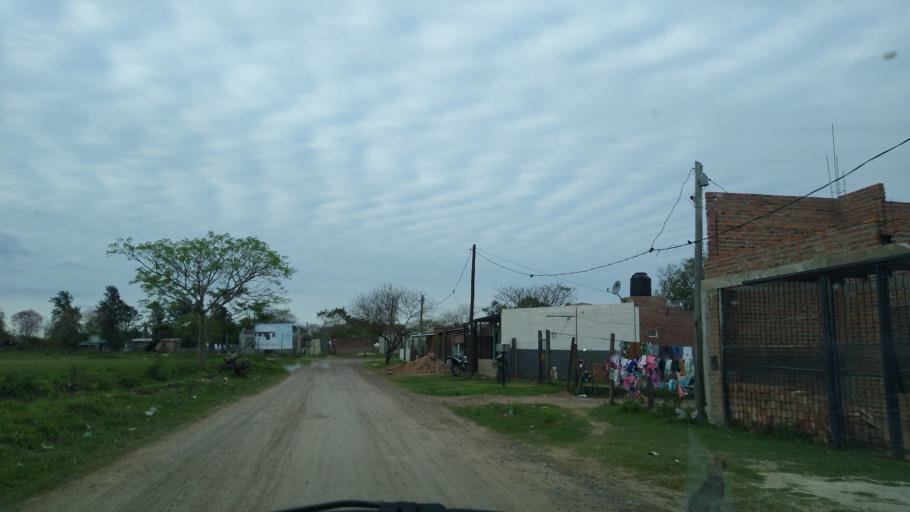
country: AR
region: Chaco
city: Fontana
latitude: -27.4023
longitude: -59.0391
